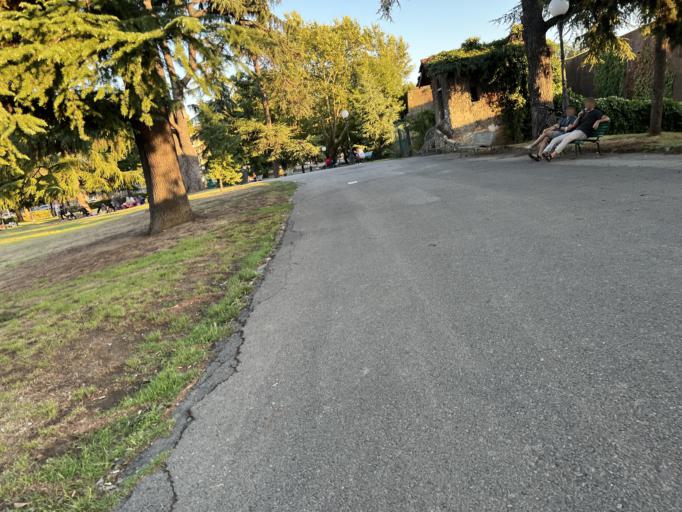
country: IT
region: Tuscany
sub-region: Province of Florence
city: Florence
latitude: 43.7821
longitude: 11.2512
